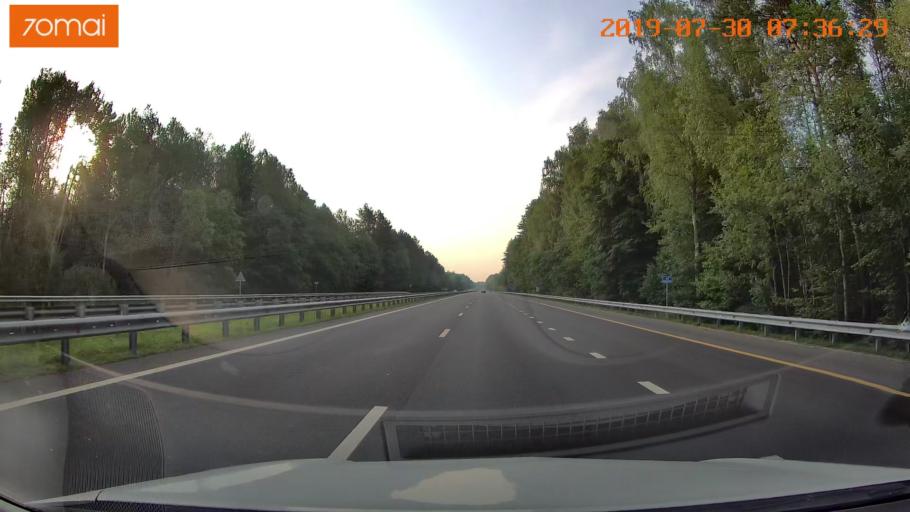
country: RU
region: Kaliningrad
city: Gvardeysk
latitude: 54.6641
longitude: 21.1254
